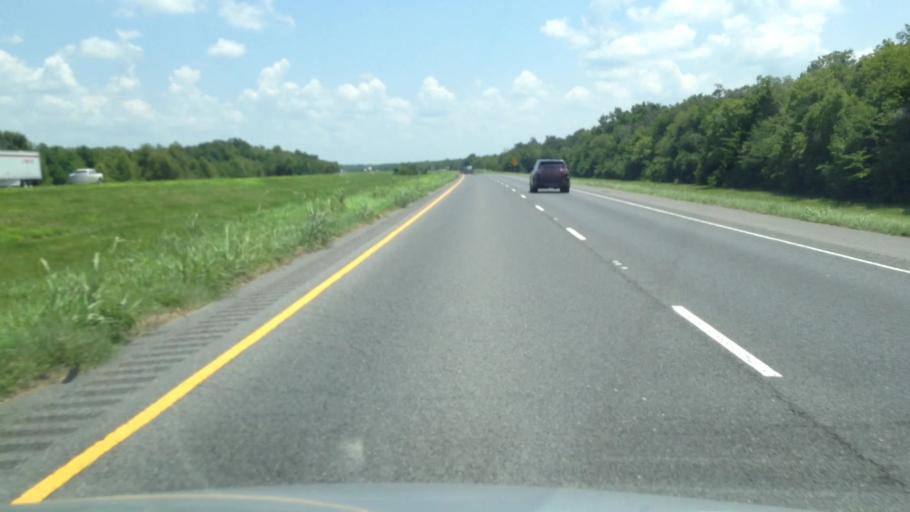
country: US
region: Louisiana
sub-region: Evangeline Parish
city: Ville Platte
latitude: 30.8156
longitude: -92.2204
